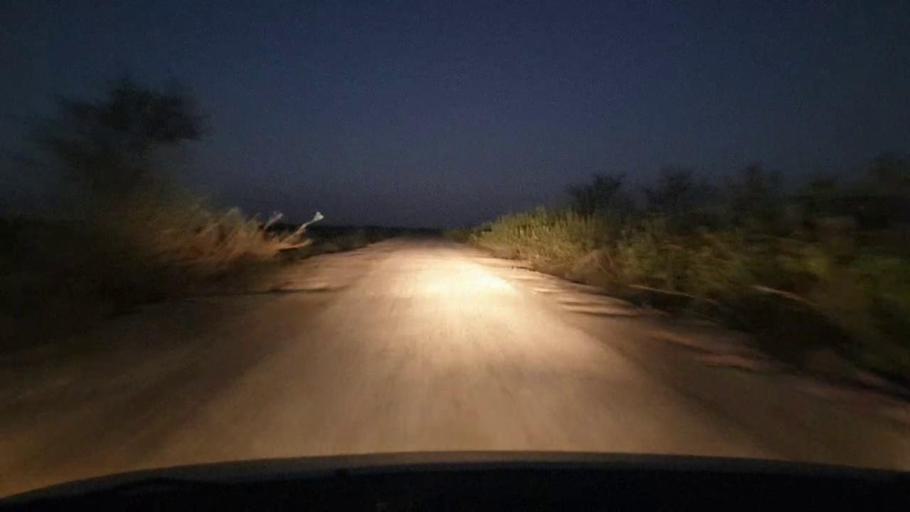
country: PK
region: Sindh
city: Phulji
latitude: 26.9164
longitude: 67.4813
